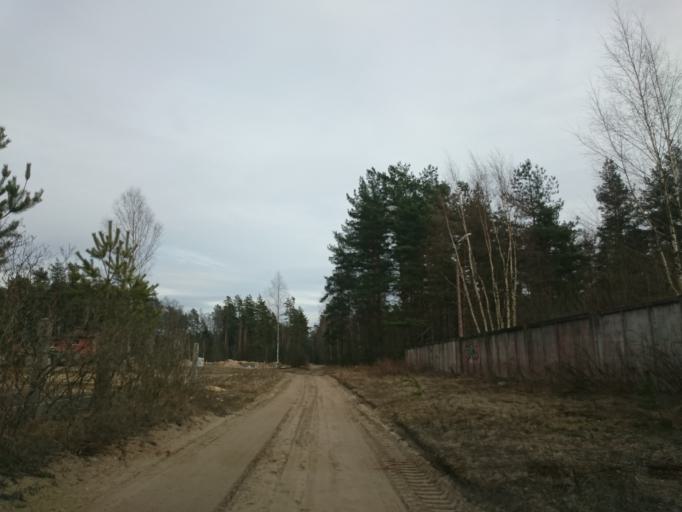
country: LV
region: Garkalne
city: Garkalne
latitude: 57.0141
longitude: 24.3969
